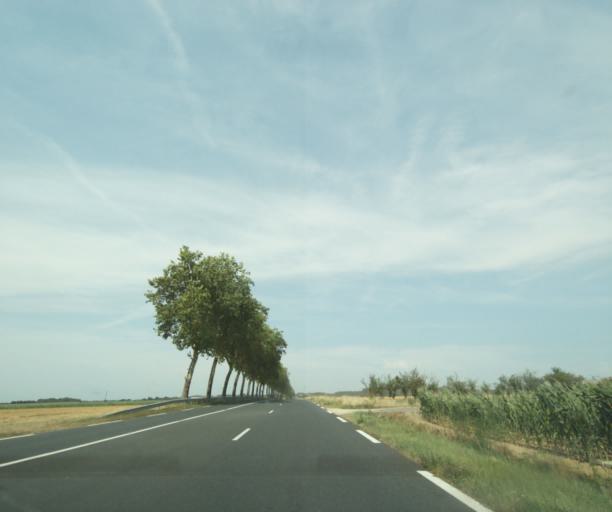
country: FR
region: Centre
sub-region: Departement d'Indre-et-Loire
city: Sainte-Maure-de-Touraine
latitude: 47.1229
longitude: 0.6251
